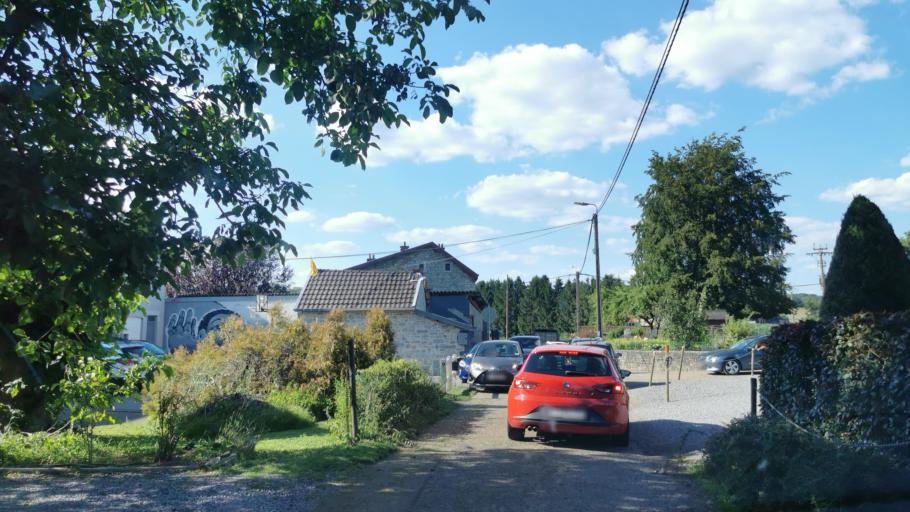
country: BE
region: Wallonia
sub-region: Province de Liege
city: Aywaille
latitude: 50.4956
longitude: 5.7102
